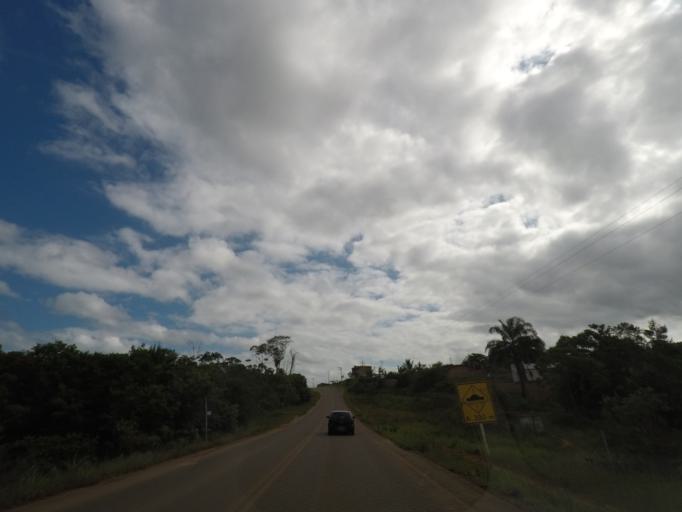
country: BR
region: Bahia
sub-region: Itacare
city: Itacare
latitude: -14.2110
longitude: -39.1008
